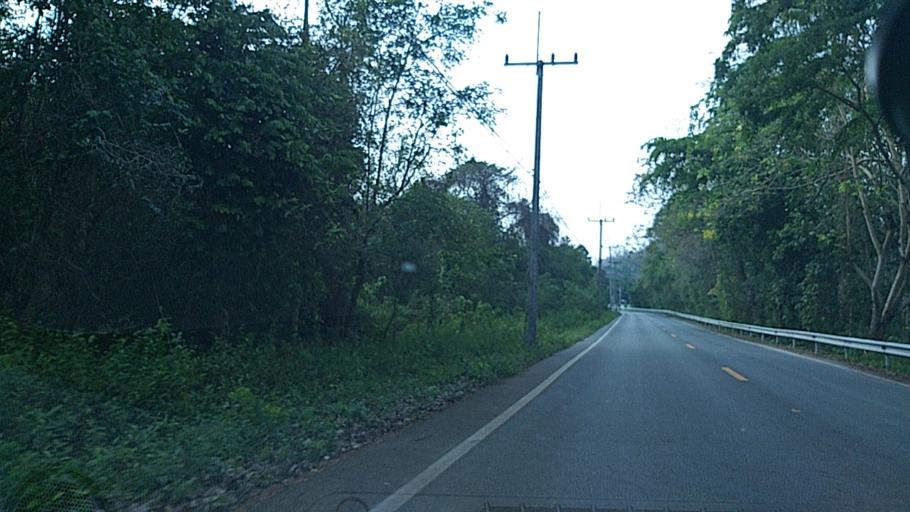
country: TH
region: Sara Buri
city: Saraburi
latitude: 14.4529
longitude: 100.9529
